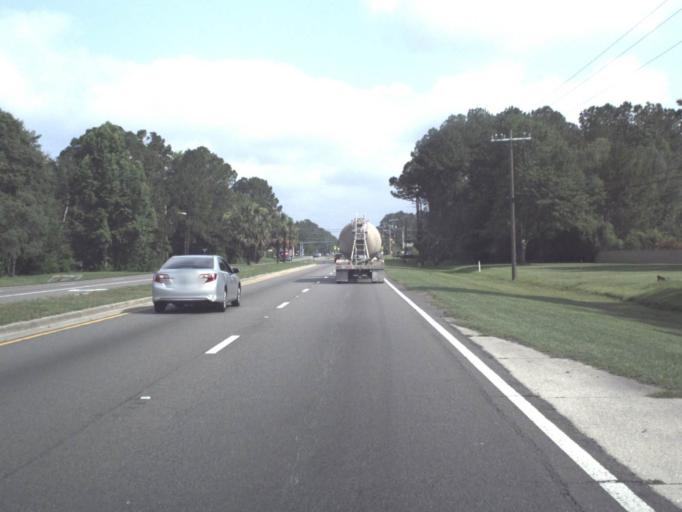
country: US
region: Florida
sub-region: Duval County
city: Jacksonville
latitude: 30.3832
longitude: -81.7311
